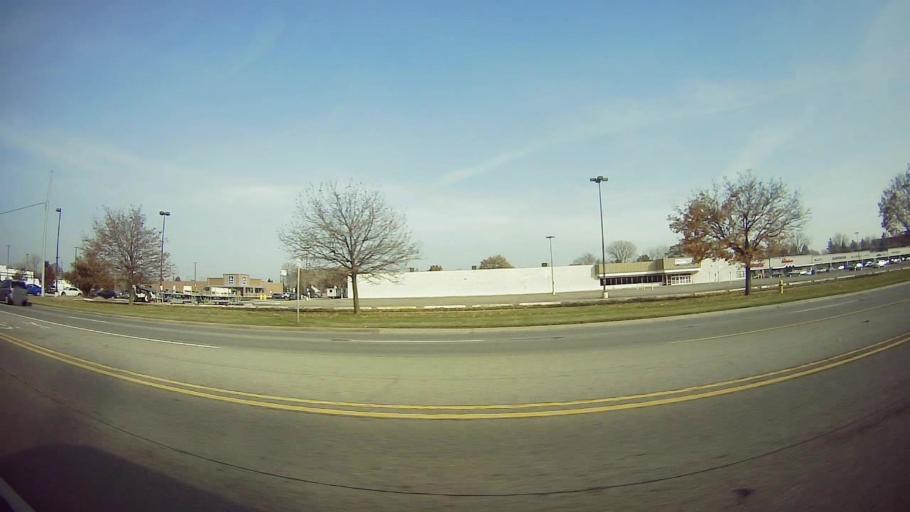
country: US
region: Michigan
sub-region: Oakland County
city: Southfield
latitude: 42.4847
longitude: -83.2023
